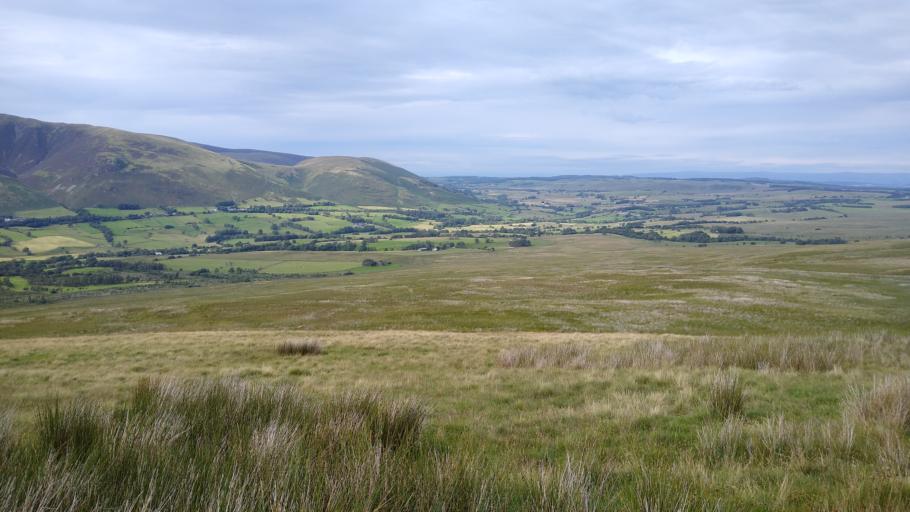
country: GB
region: England
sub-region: Cumbria
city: Keswick
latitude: 54.6026
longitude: -3.0223
